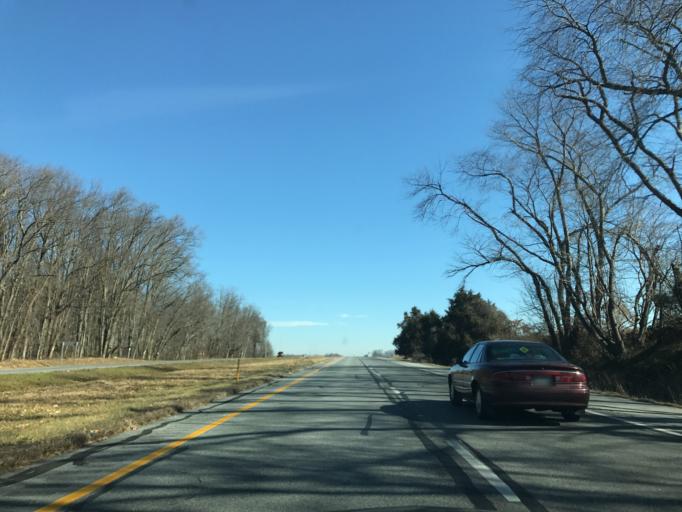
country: US
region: Delaware
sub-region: New Castle County
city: Middletown
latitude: 39.3794
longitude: -75.8054
